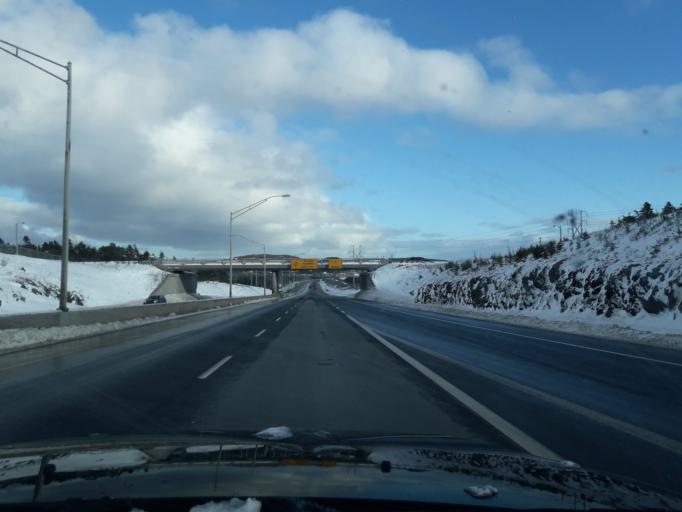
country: CA
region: Newfoundland and Labrador
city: St. John's
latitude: 47.6131
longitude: -52.7080
